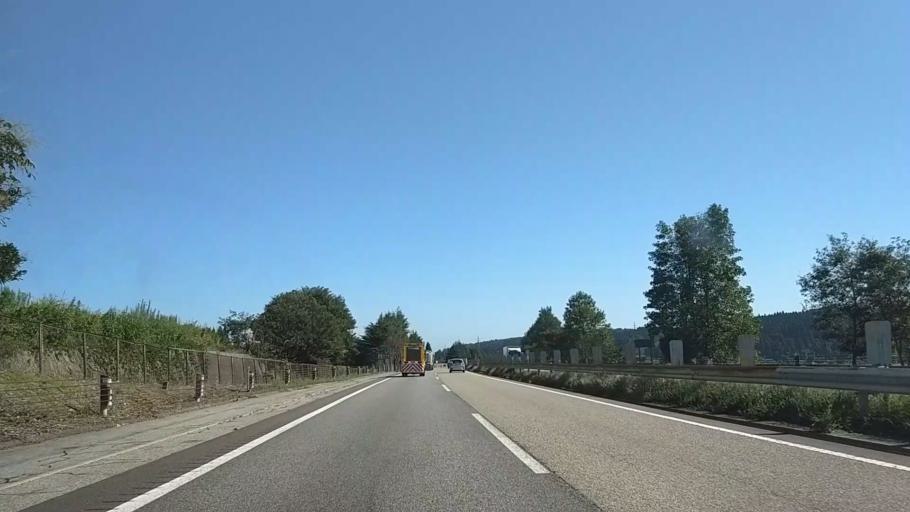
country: JP
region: Toyama
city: Takaoka
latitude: 36.6762
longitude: 137.0356
